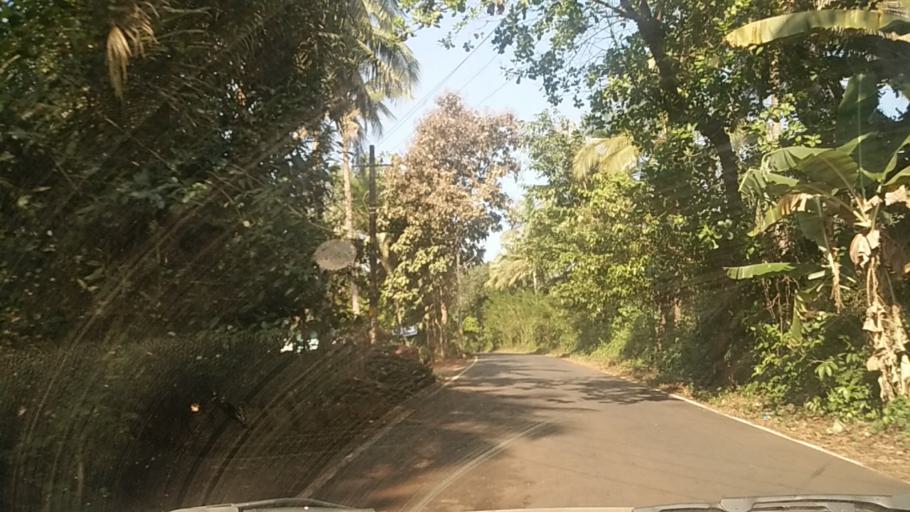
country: IN
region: Goa
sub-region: South Goa
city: Sanguem
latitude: 15.1742
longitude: 74.2326
